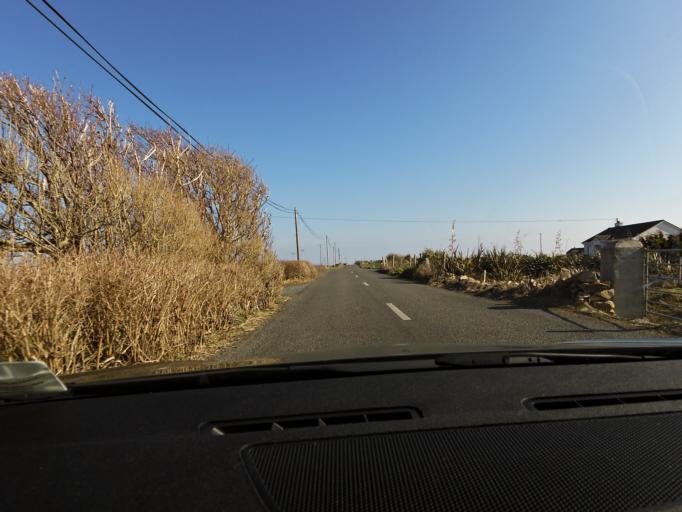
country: IE
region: Connaught
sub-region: County Galway
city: Clifden
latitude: 53.4198
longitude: -10.0617
